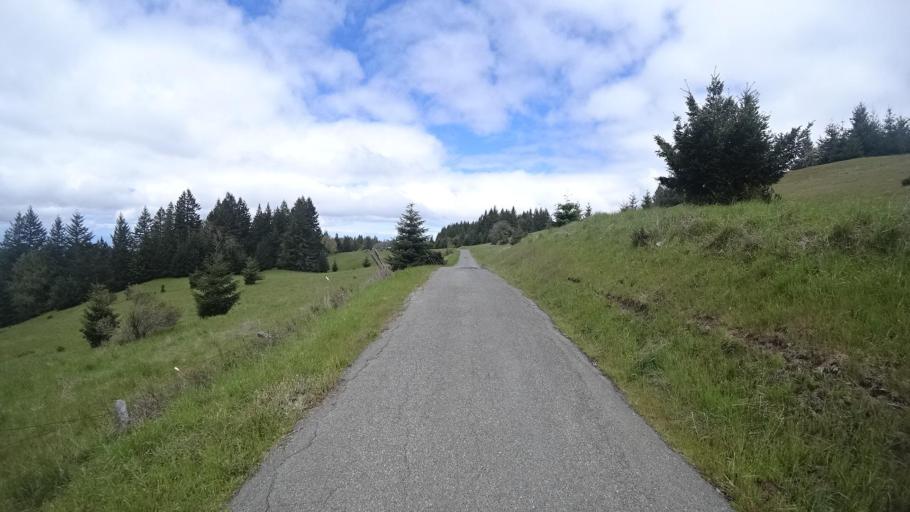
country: US
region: California
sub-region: Humboldt County
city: Blue Lake
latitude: 40.7889
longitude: -123.9666
